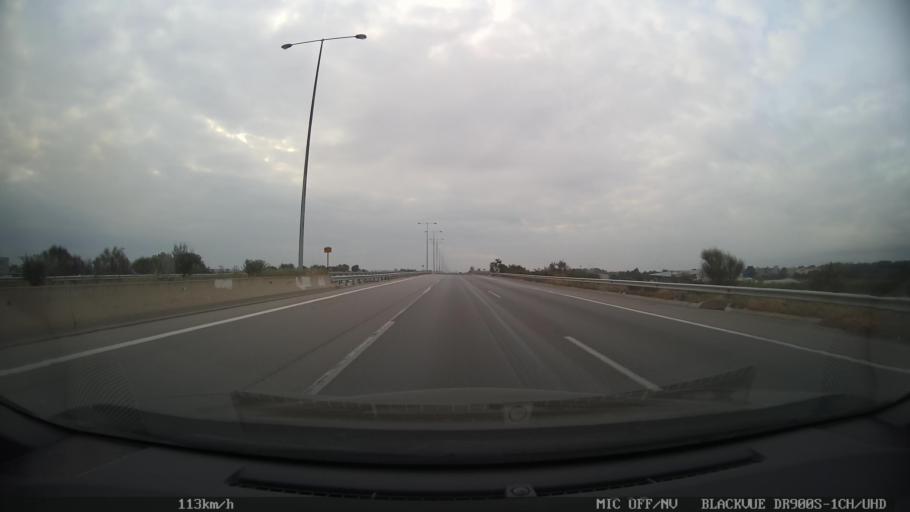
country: GR
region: Central Macedonia
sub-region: Nomos Thessalonikis
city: Nea Magnisia
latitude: 40.6696
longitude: 22.8341
